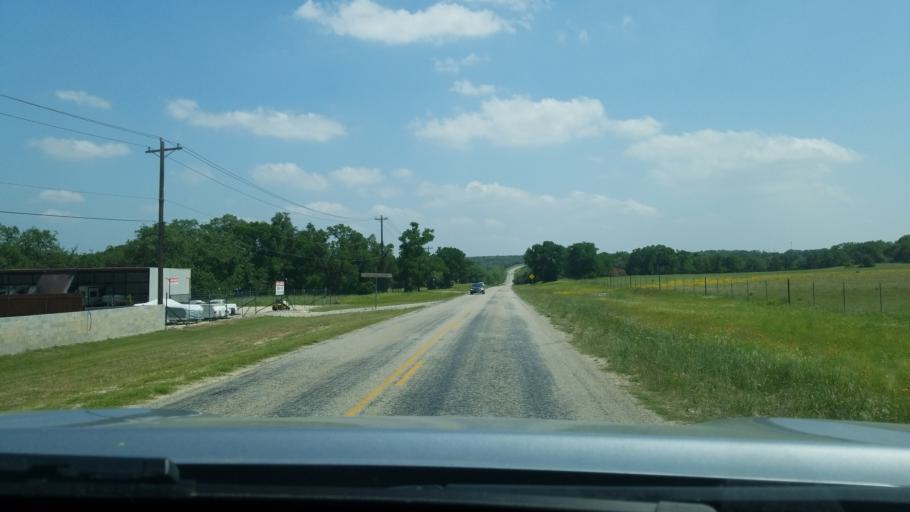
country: US
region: Texas
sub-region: Bexar County
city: Fair Oaks Ranch
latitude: 29.8968
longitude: -98.5611
